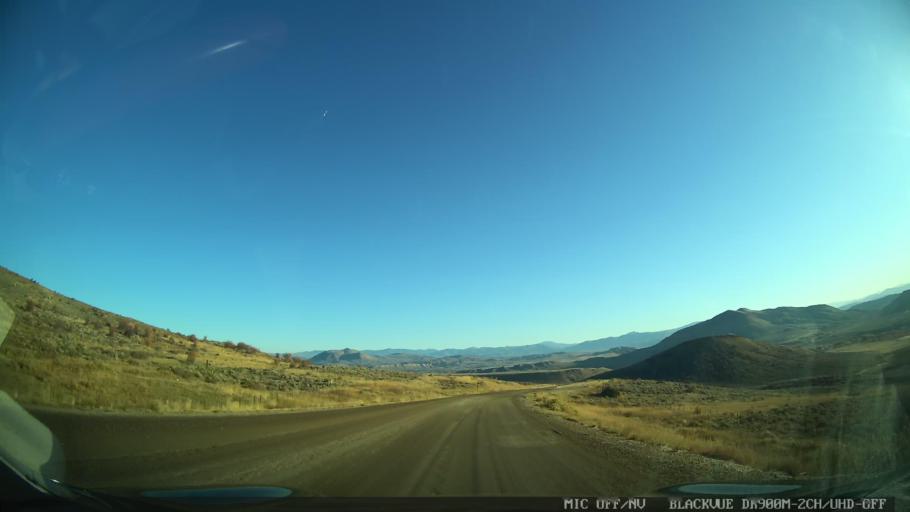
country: US
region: Colorado
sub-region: Grand County
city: Kremmling
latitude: 40.0052
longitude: -106.4066
